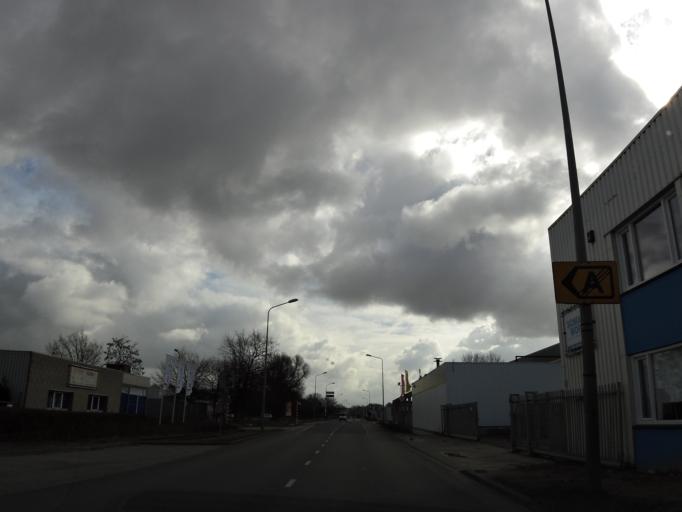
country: NL
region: Limburg
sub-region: Gemeente Maastricht
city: Maastricht
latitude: 50.8751
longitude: 5.7081
